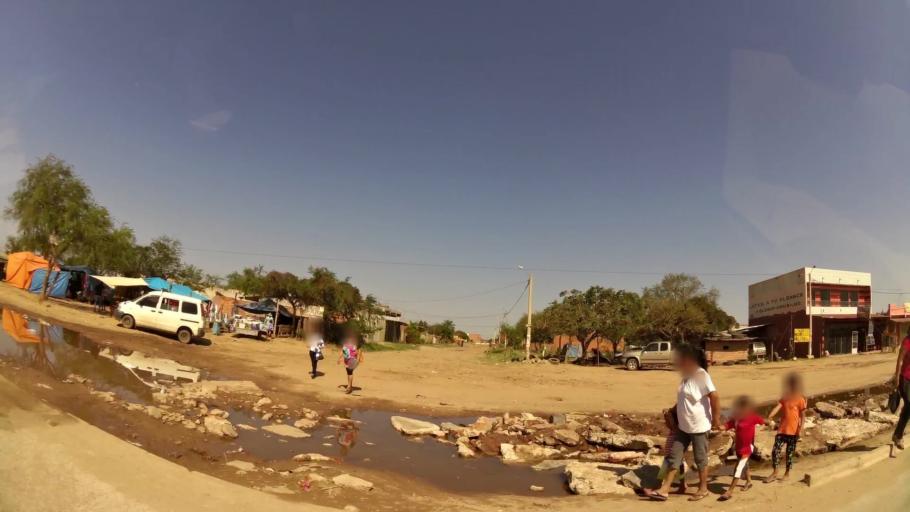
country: BO
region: Santa Cruz
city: Cotoca
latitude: -17.7276
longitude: -63.0886
